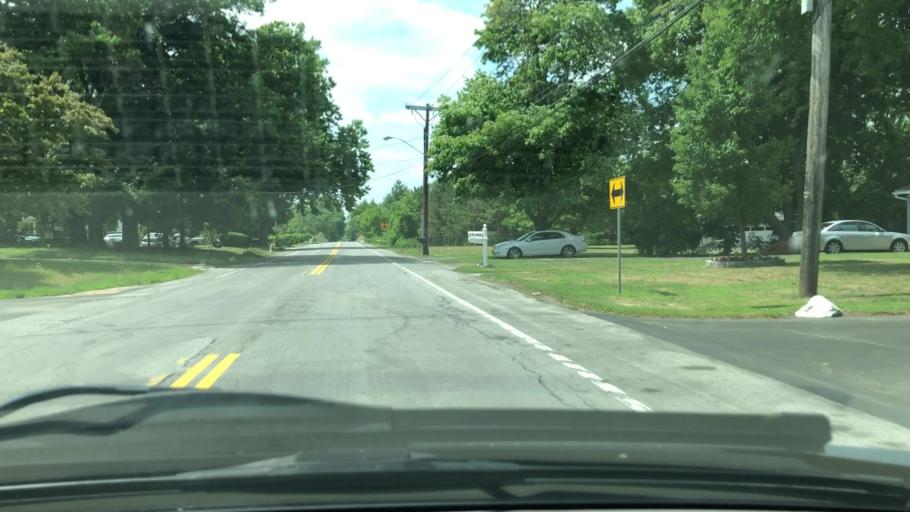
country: US
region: New York
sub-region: Monroe County
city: North Gates
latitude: 43.1256
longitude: -77.7268
